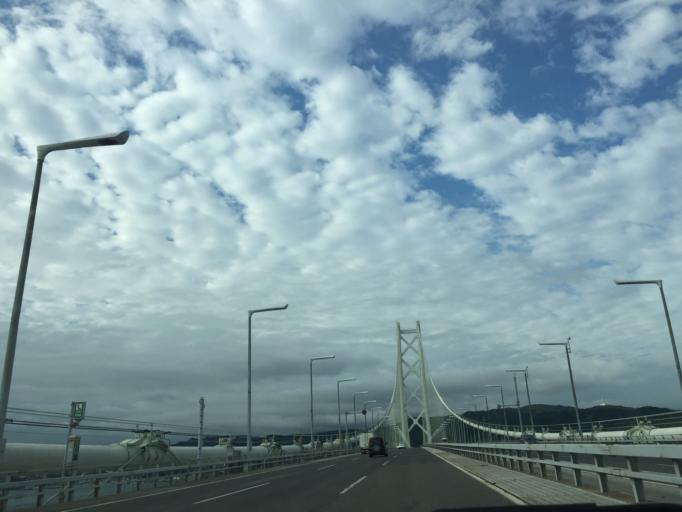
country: JP
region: Hyogo
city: Akashi
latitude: 34.6172
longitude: 135.0216
